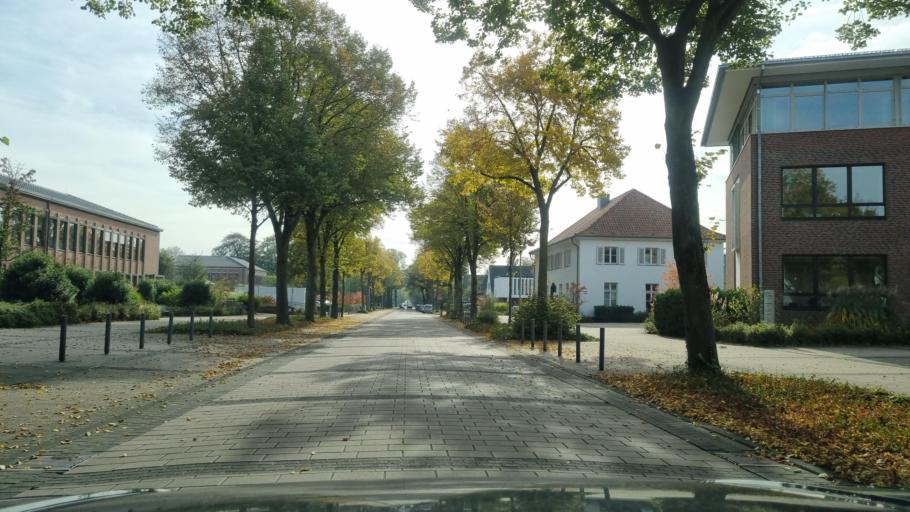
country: DE
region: North Rhine-Westphalia
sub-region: Regierungsbezirk Dusseldorf
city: Kleve
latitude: 51.7822
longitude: 6.1374
